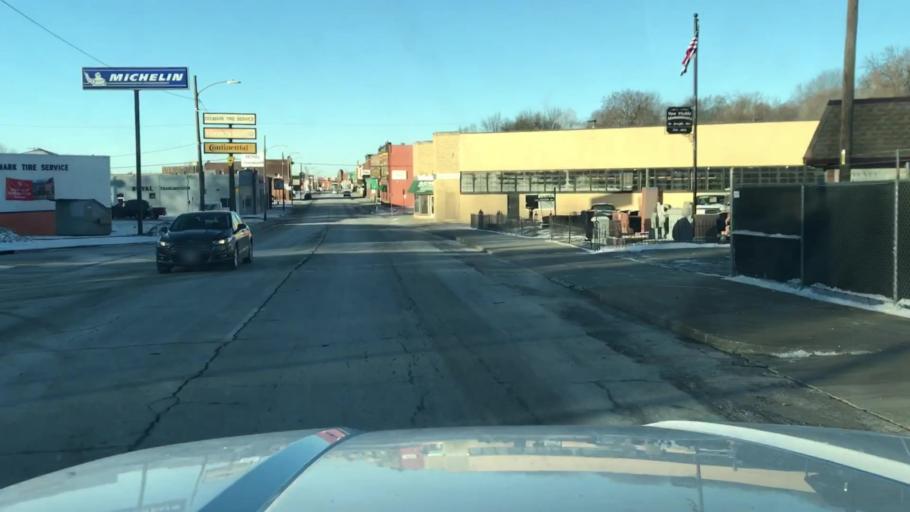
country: US
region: Missouri
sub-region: Buchanan County
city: Saint Joseph
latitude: 39.7731
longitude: -94.8393
